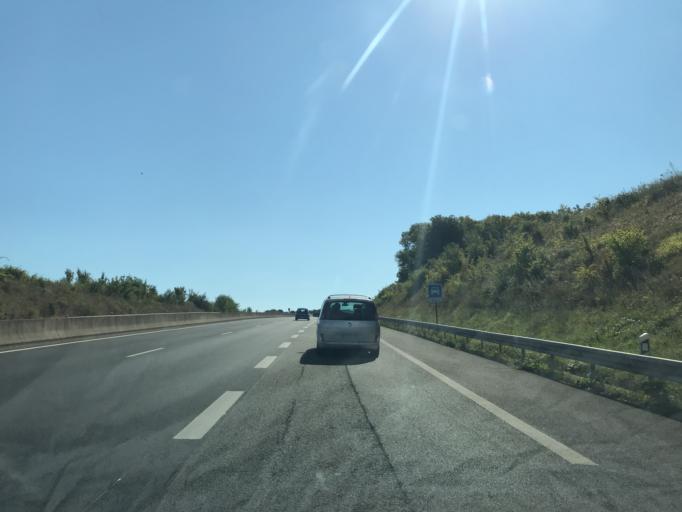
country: FR
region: Ile-de-France
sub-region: Departement du Val-d'Oise
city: Magny-en-Vexin
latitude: 49.1481
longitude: 1.7924
